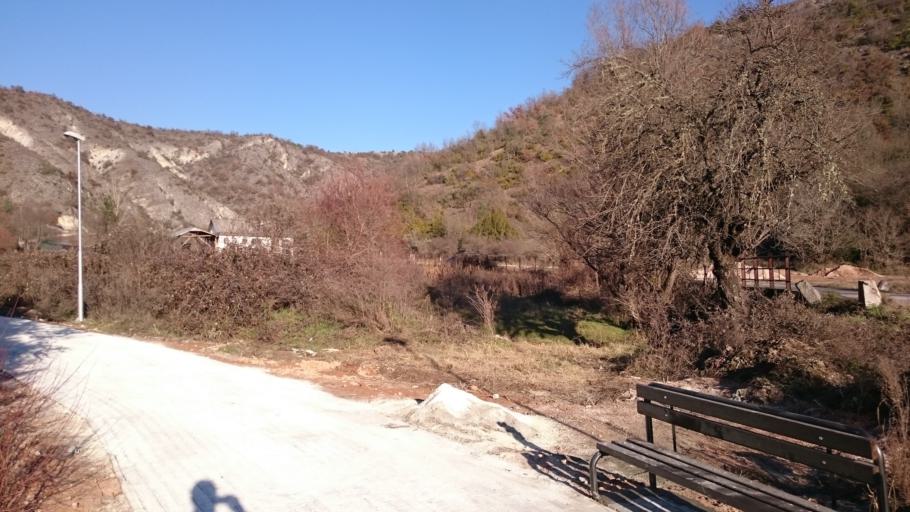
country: MK
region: Makedonski Brod
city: Makedonski Brod
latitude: 41.5433
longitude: 21.2458
